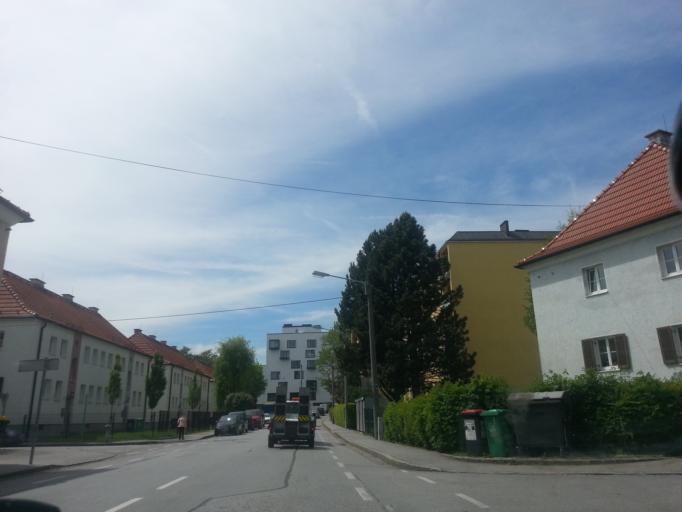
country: AT
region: Salzburg
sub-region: Politischer Bezirk Salzburg-Umgebung
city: Bergheim
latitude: 47.8198
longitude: 13.0200
